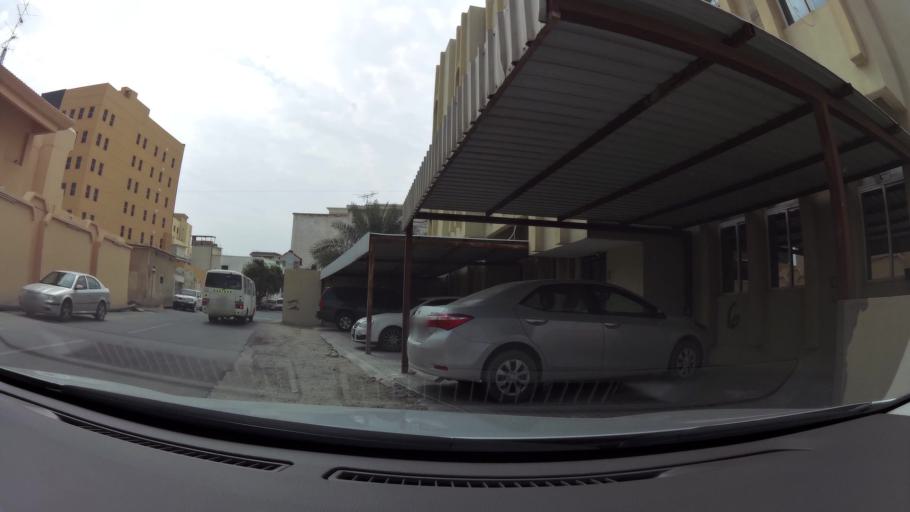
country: QA
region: Baladiyat ad Dawhah
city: Doha
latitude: 25.3046
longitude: 51.4982
